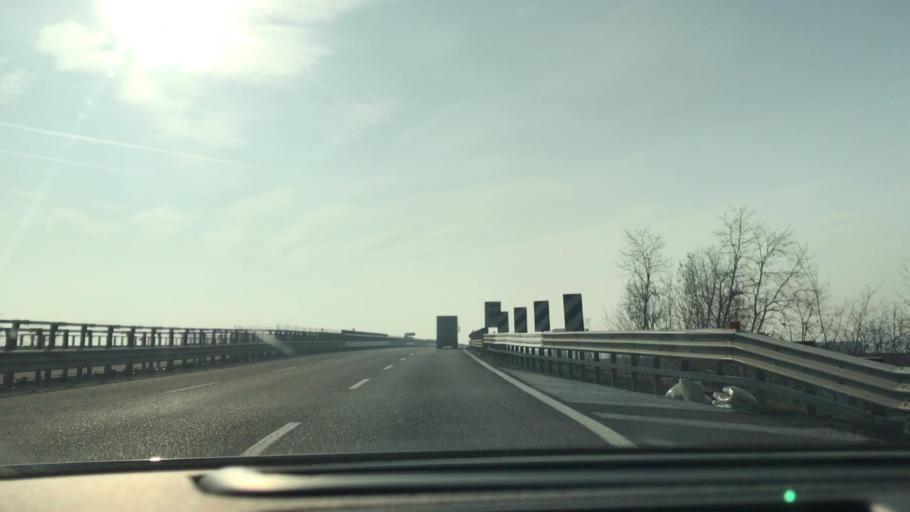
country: IT
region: Piedmont
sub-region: Provincia di Alessandria
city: Alessandria
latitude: 44.9227
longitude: 8.5774
